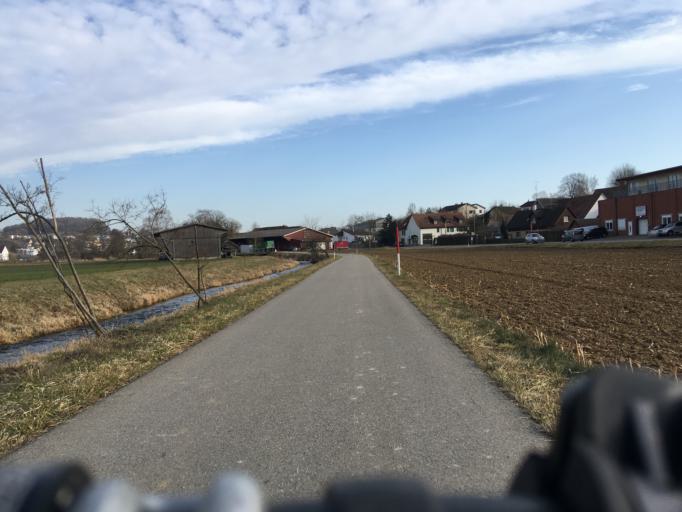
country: CH
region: Schaffhausen
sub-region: Bezirk Reiat
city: Thayngen
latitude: 47.7550
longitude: 8.6926
